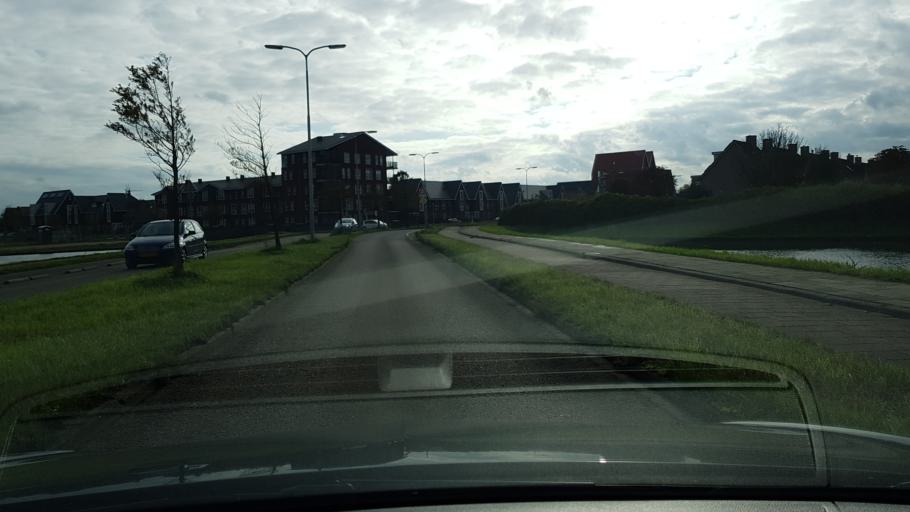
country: NL
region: South Holland
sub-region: Gemeente Hillegom
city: Hillegom
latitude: 52.2983
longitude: 4.5939
